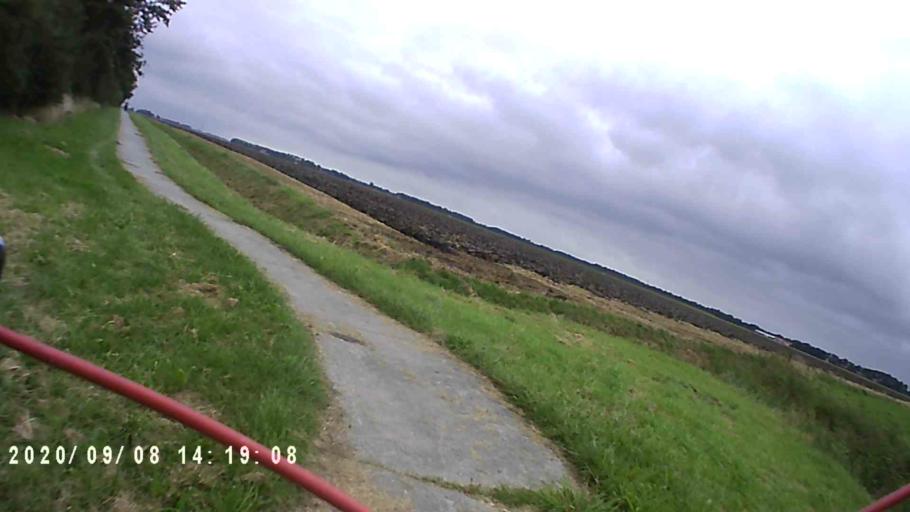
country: NL
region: Groningen
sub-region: Gemeente Slochteren
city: Slochteren
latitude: 53.2087
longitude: 6.8411
